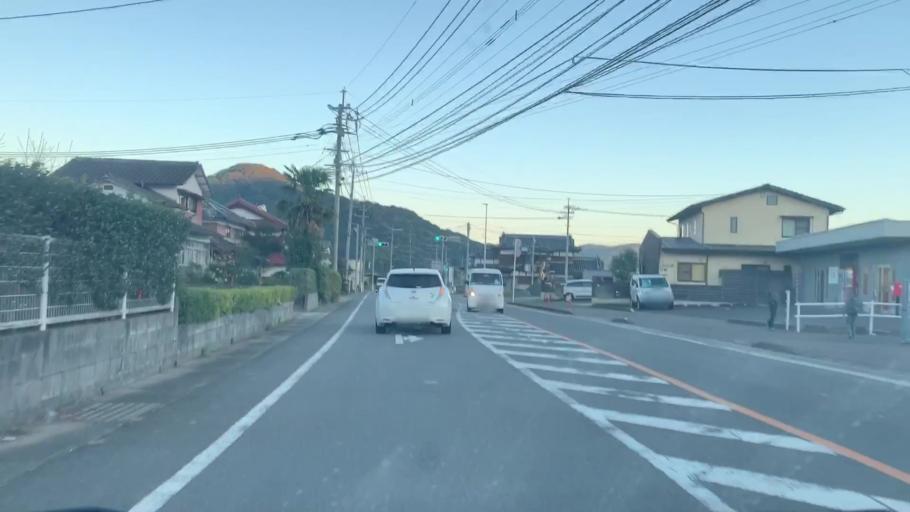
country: JP
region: Saga Prefecture
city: Takeocho-takeo
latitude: 33.2218
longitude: 130.0270
